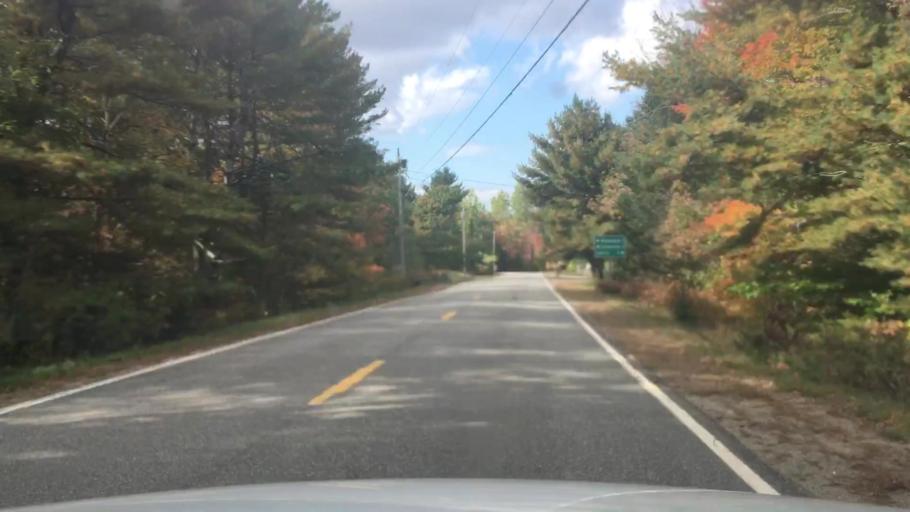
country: US
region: Maine
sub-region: Knox County
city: Washington
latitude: 44.3194
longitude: -69.3589
